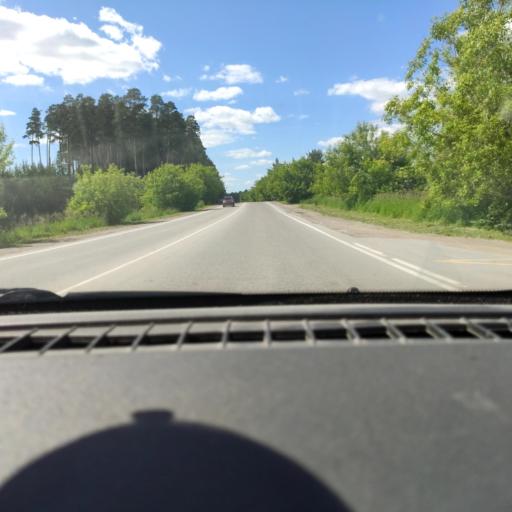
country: RU
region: Perm
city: Krasnokamsk
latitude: 58.0762
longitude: 55.6894
